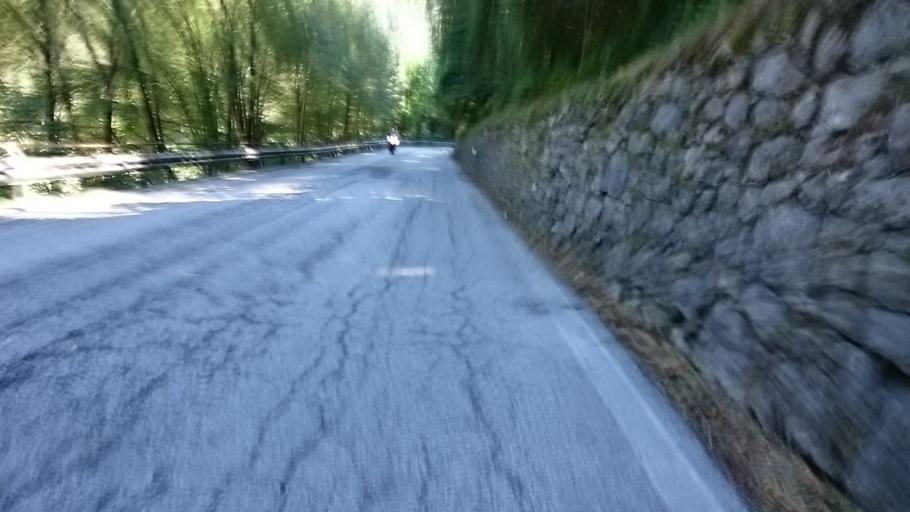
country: IT
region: Veneto
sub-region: Provincia di Belluno
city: Ospitale di Cadore
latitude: 46.3088
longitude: 12.3241
